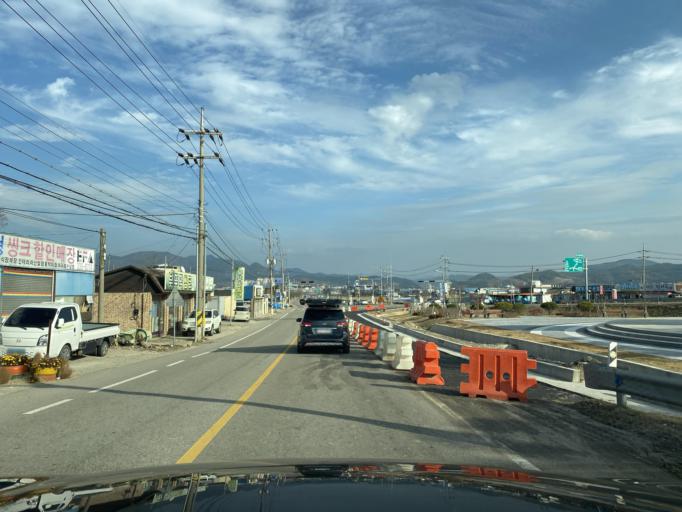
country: KR
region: Chungcheongnam-do
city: Yesan
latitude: 36.6850
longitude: 126.8054
